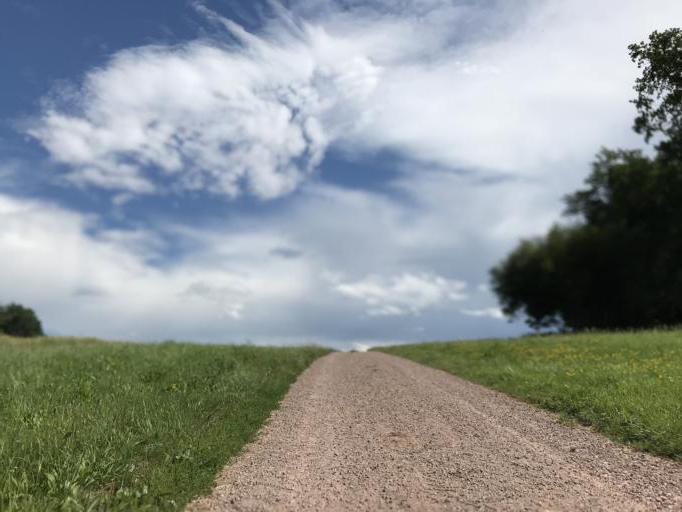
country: DE
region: Baden-Wuerttemberg
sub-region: Freiburg Region
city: Schopfheim
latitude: 47.6348
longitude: 7.8311
